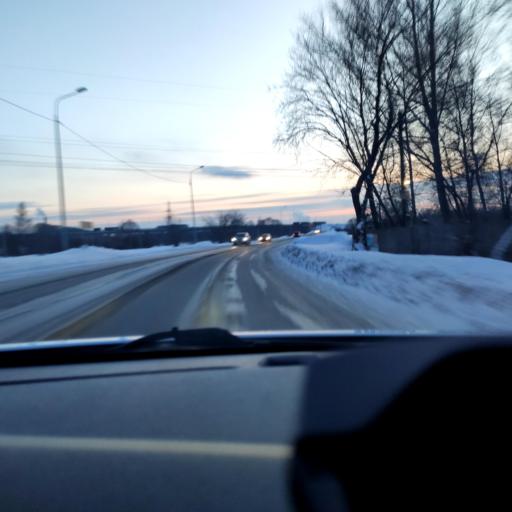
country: RU
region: Tatarstan
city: Vysokaya Gora
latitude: 55.8881
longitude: 49.2429
